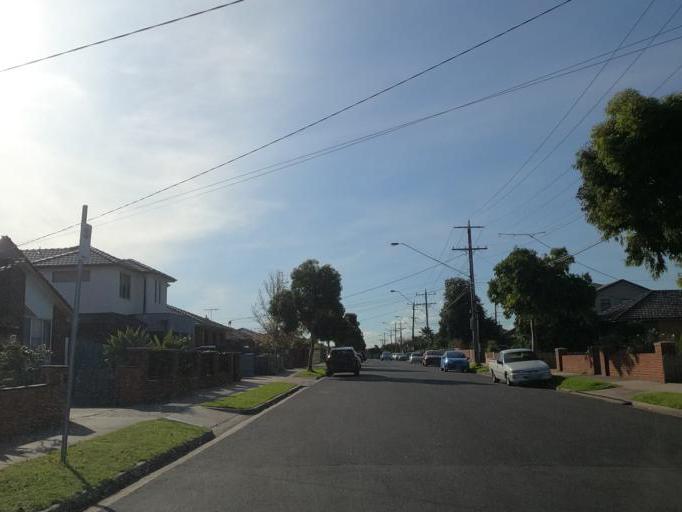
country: AU
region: Victoria
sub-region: Moonee Valley
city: Airport West
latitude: -37.7227
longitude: 144.8821
